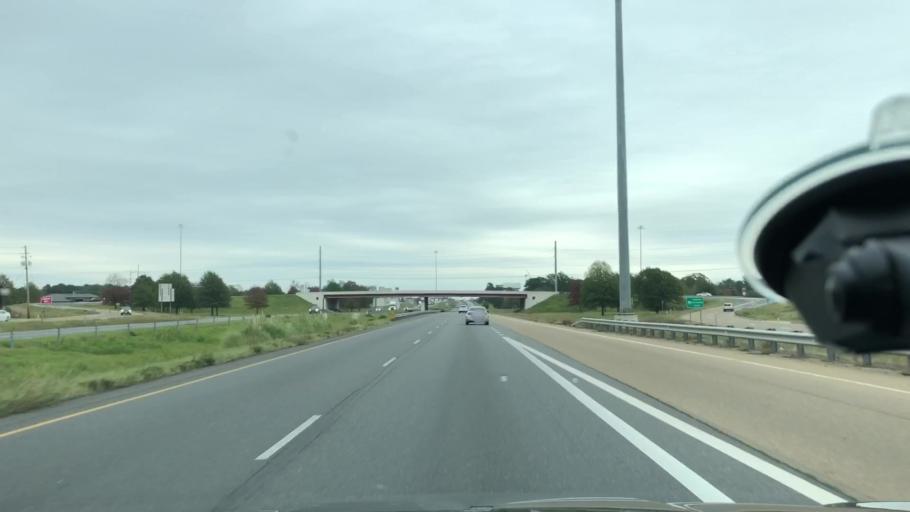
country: US
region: Arkansas
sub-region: Miller County
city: Texarkana
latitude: 33.4705
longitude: -94.0322
